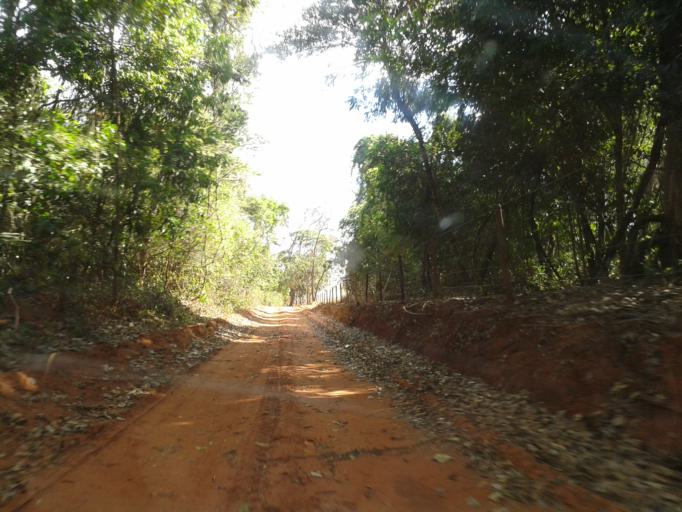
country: BR
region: Minas Gerais
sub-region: Centralina
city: Centralina
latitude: -18.7571
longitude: -49.0803
